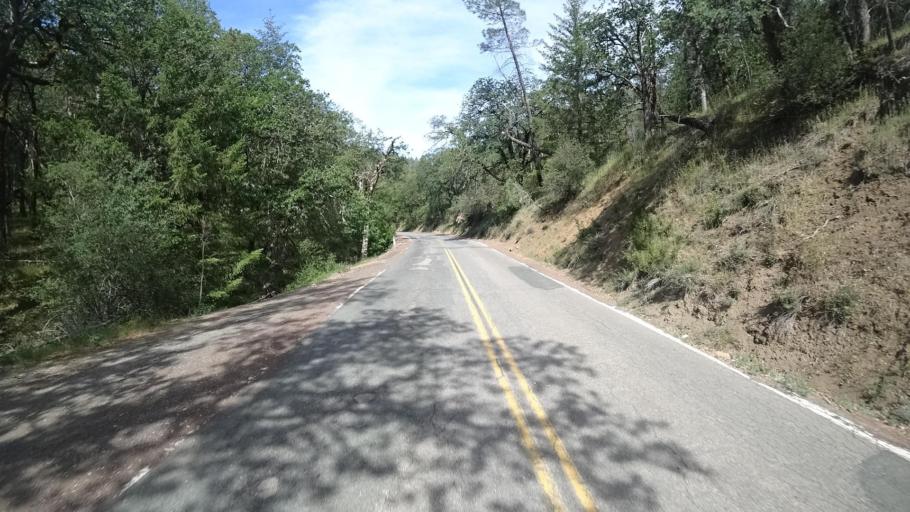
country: US
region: California
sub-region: Lake County
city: Cobb
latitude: 38.8557
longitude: -122.7371
